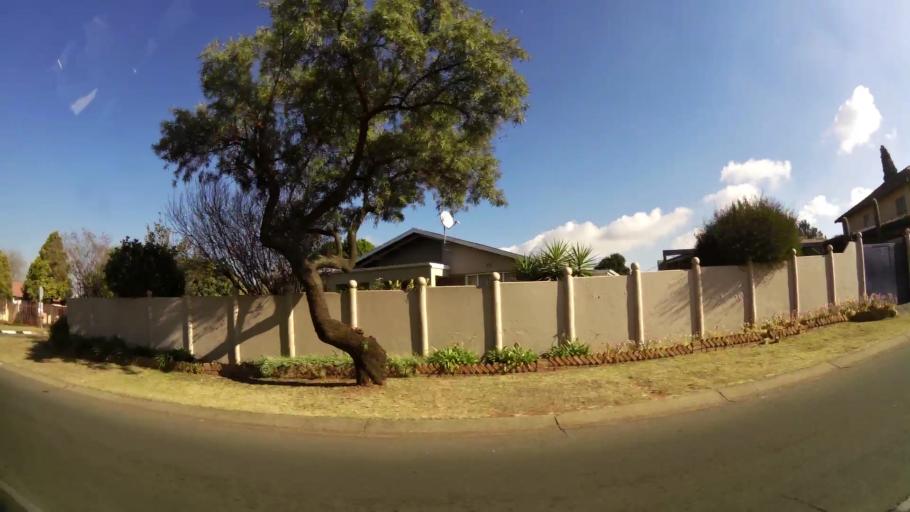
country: ZA
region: Gauteng
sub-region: City of Johannesburg Metropolitan Municipality
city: Roodepoort
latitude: -26.1575
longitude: 27.8275
